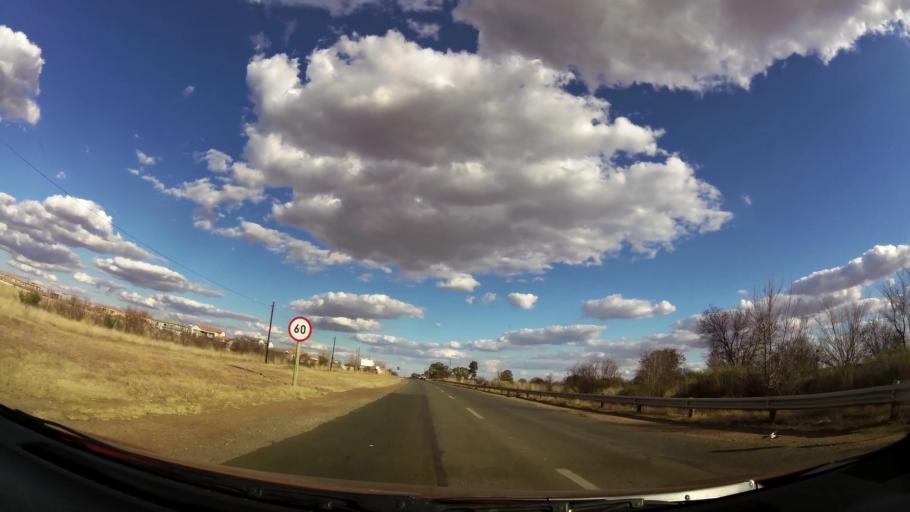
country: ZA
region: North-West
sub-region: Dr Kenneth Kaunda District Municipality
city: Potchefstroom
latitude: -26.6627
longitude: 27.1050
